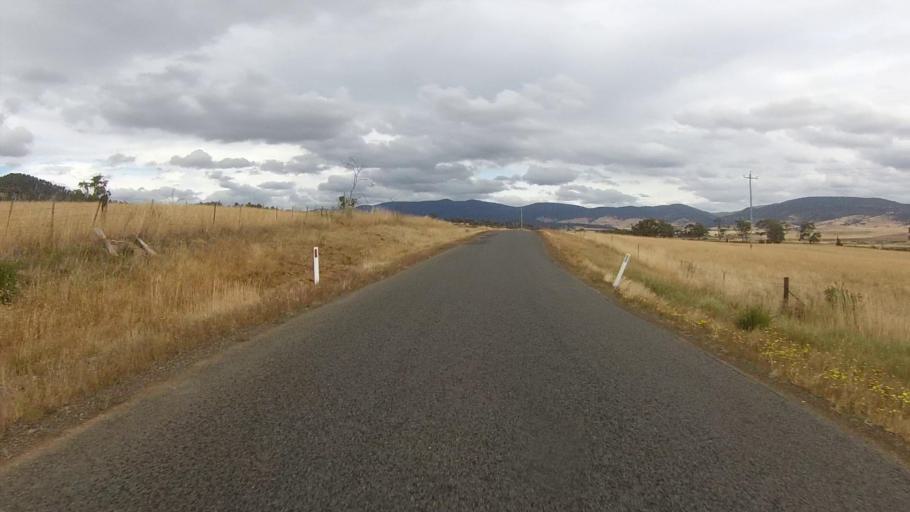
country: AU
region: Tasmania
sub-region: Northern Midlands
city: Evandale
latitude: -41.7997
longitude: 147.7494
